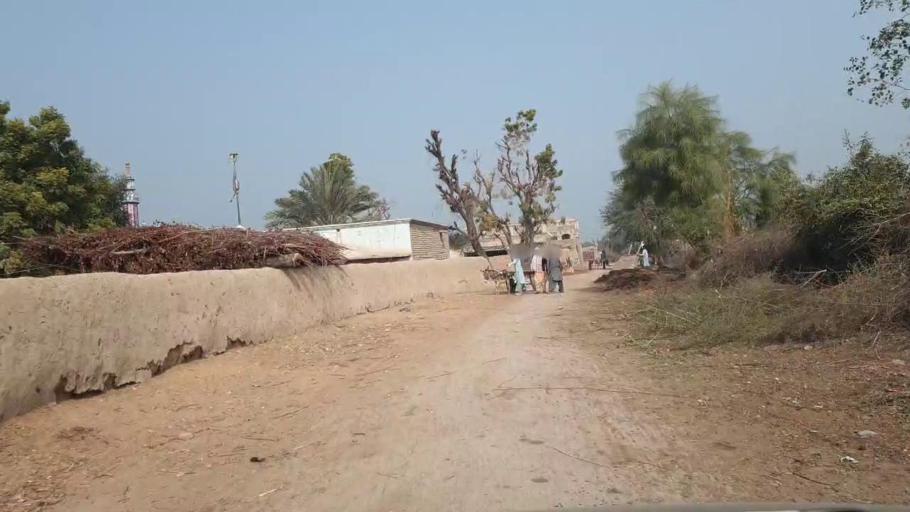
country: PK
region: Sindh
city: Bhit Shah
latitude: 25.8458
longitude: 68.4748
